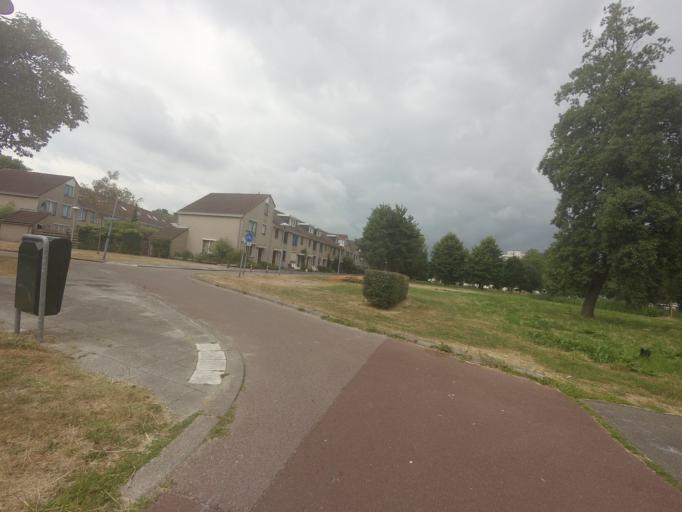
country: NL
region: Utrecht
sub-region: Gemeente Utrecht
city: Utrecht
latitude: 52.1162
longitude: 5.0937
